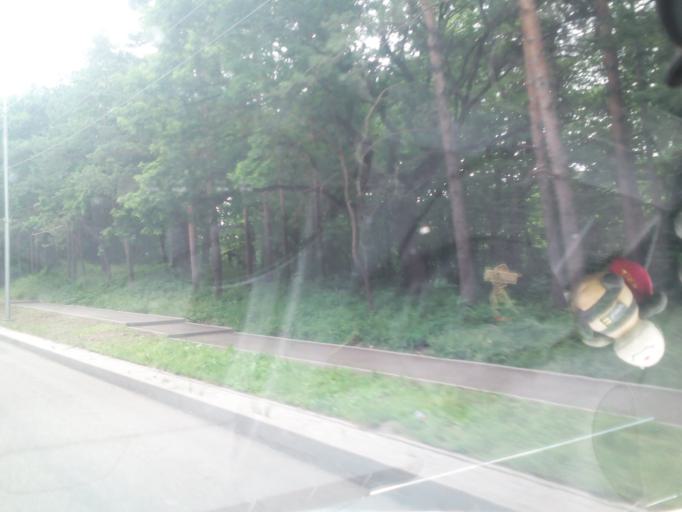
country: RU
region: Stavropol'skiy
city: Zheleznovodsk
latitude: 44.1383
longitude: 43.0145
